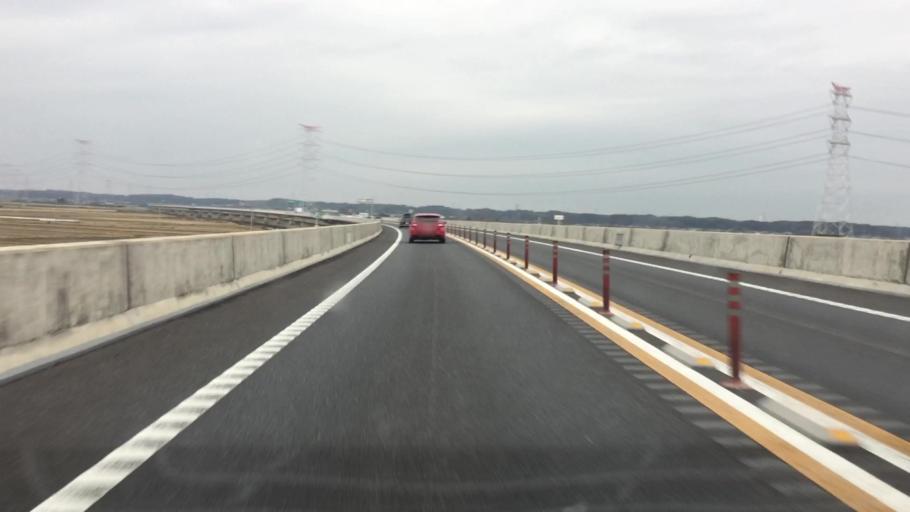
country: JP
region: Ibaraki
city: Inashiki
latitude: 35.9100
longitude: 140.3699
